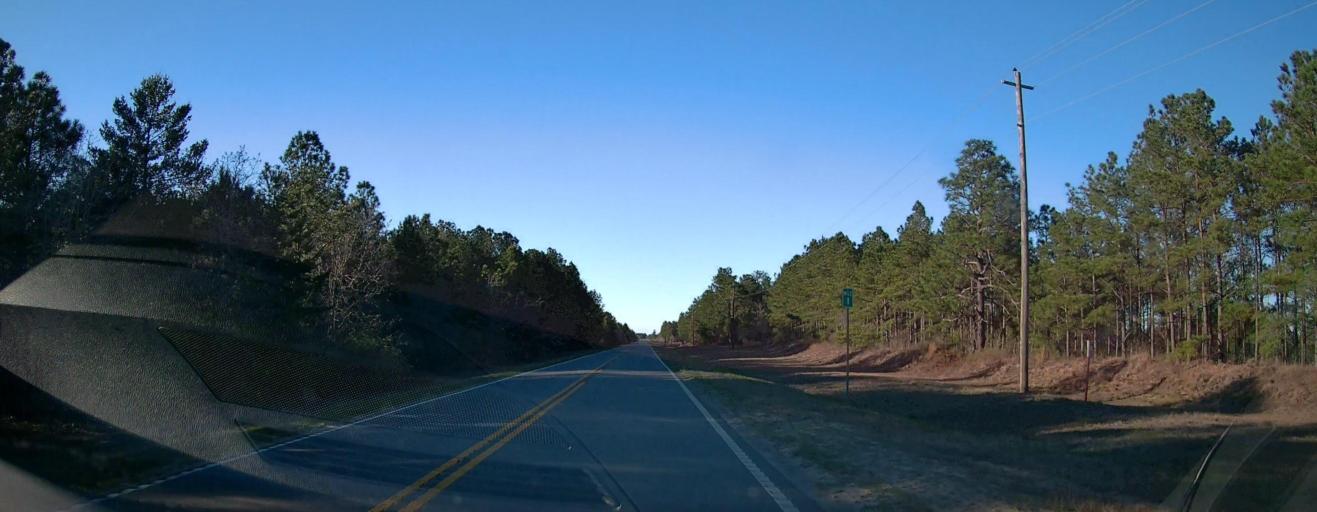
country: US
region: Georgia
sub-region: Talbot County
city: Talbotton
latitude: 32.5735
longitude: -84.4425
